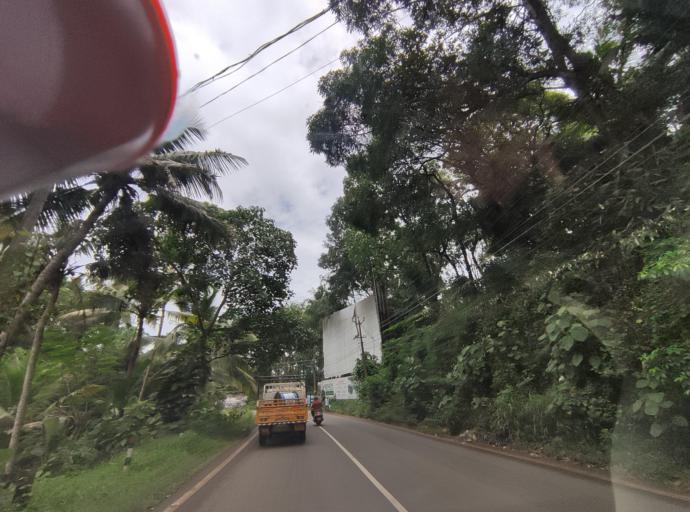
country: IN
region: Kerala
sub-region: Thiruvananthapuram
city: Nedumangad
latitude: 8.5852
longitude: 76.9477
